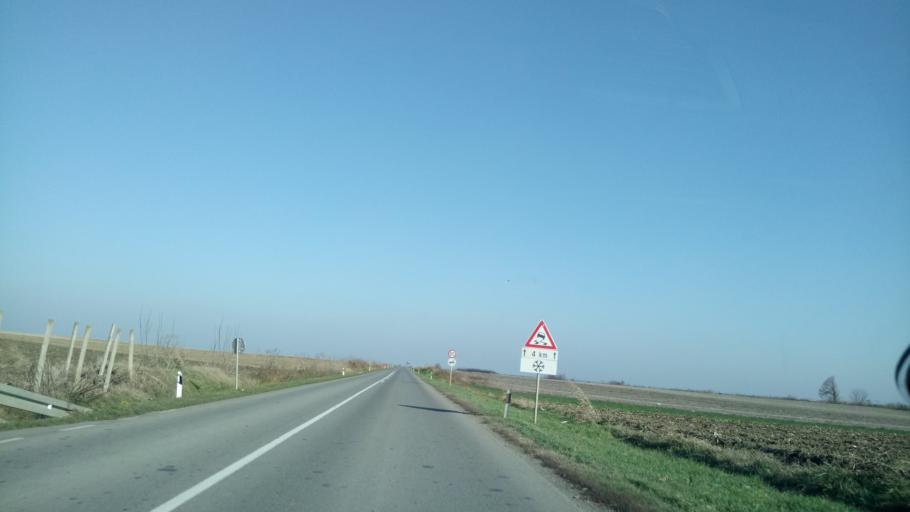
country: RS
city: Putinci
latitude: 44.9928
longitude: 19.9851
